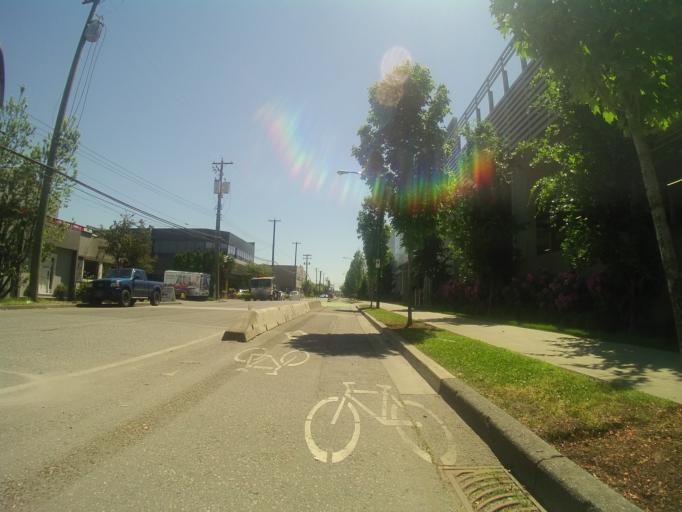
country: CA
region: British Columbia
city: Vancouver
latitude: 49.2110
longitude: -123.1067
